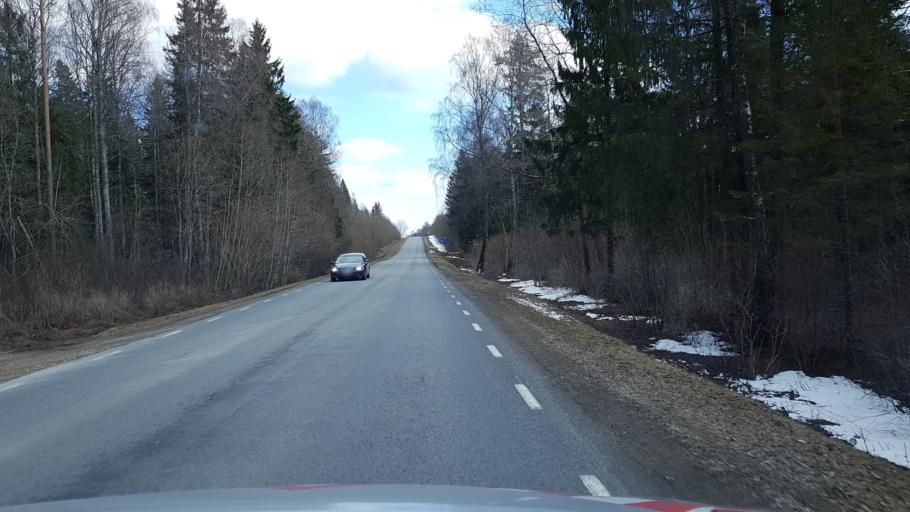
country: EE
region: Laeaene-Virumaa
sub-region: Tamsalu vald
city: Tamsalu
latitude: 59.1656
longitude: 26.0749
